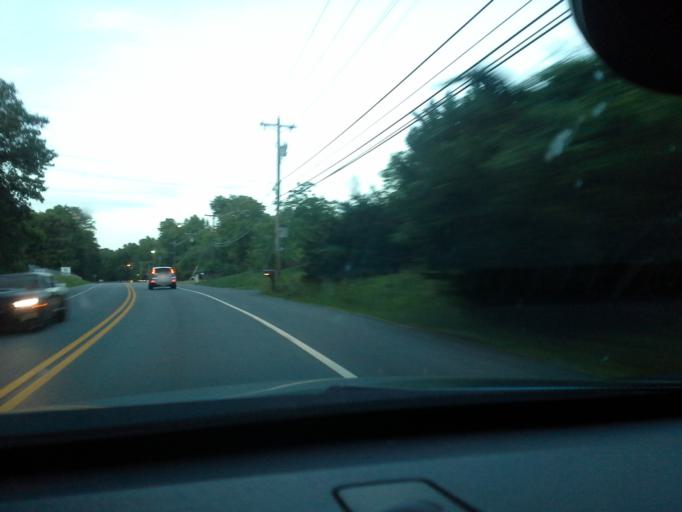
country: US
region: Maryland
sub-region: Calvert County
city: Huntingtown
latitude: 38.5853
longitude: -76.6030
